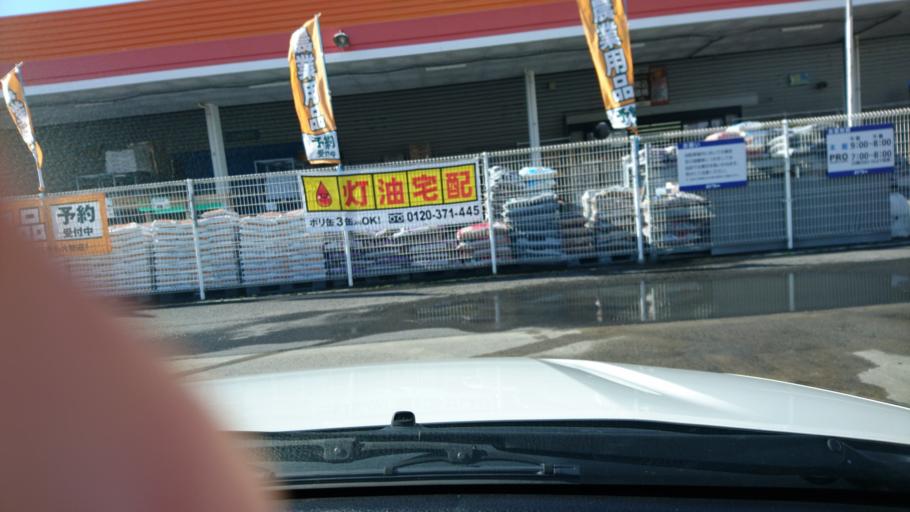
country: JP
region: Mie
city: Ueno-ebisumachi
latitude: 34.7770
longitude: 136.1227
